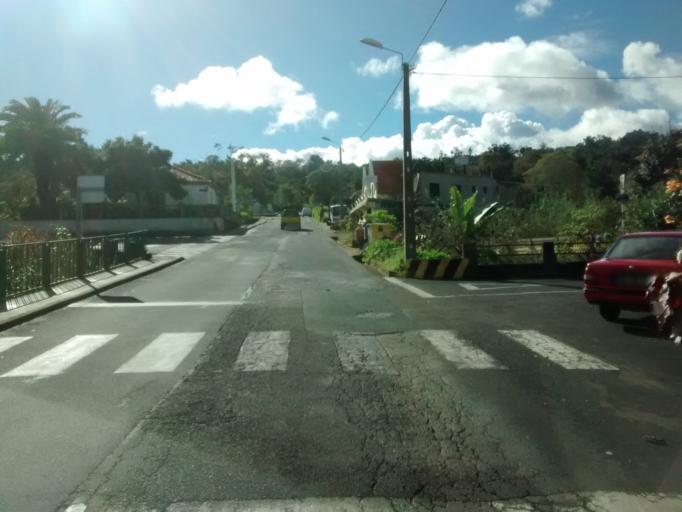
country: PT
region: Madeira
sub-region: Santana
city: Santana
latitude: 32.8040
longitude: -16.8815
